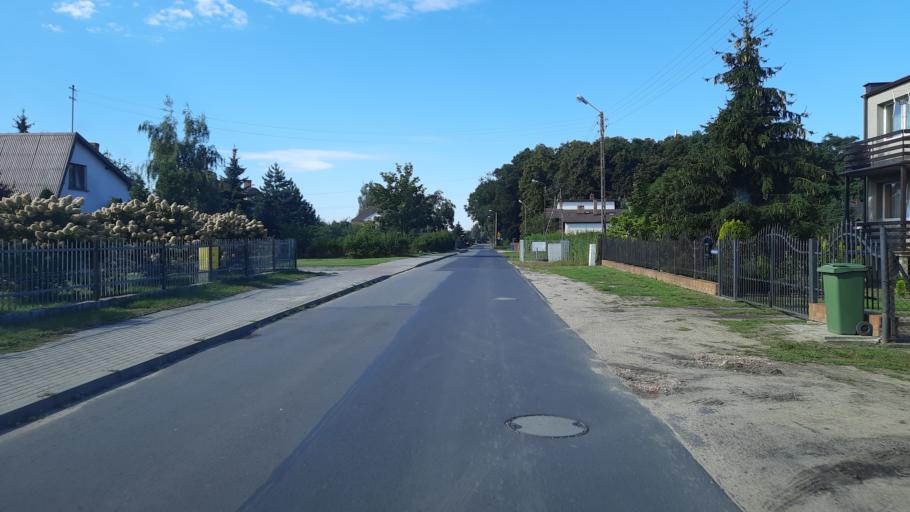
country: PL
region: Lower Silesian Voivodeship
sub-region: Powiat wroclawski
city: Dlugoleka
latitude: 51.1930
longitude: 17.1789
